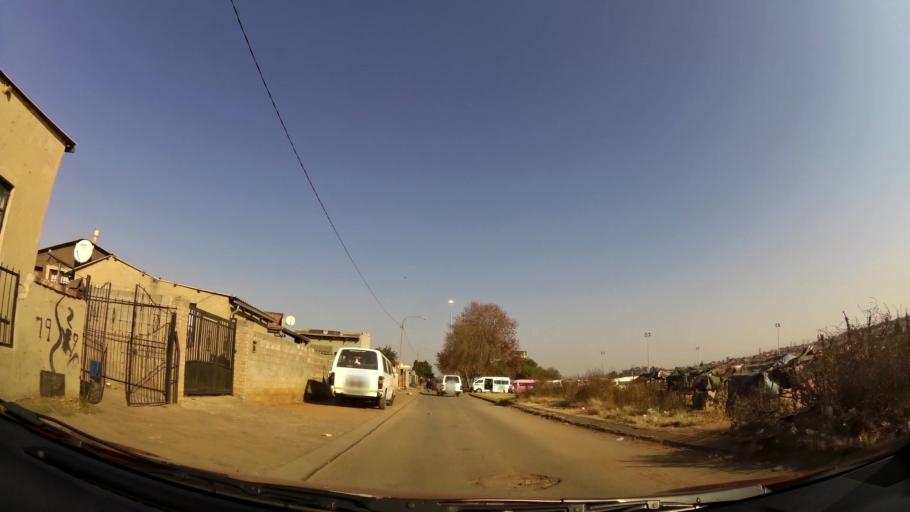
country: ZA
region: Gauteng
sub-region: City of Johannesburg Metropolitan Municipality
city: Soweto
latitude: -26.2552
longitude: 27.9384
